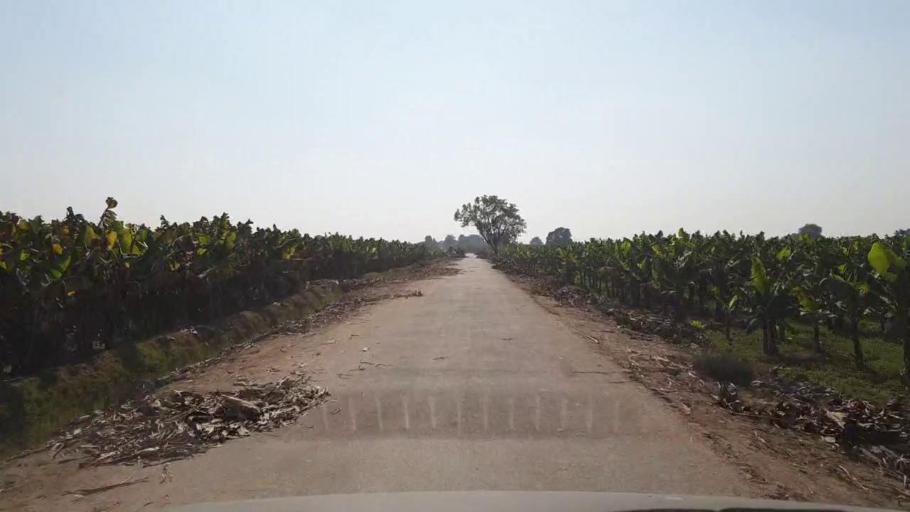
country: PK
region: Sindh
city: Tando Jam
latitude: 25.4185
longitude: 68.6313
